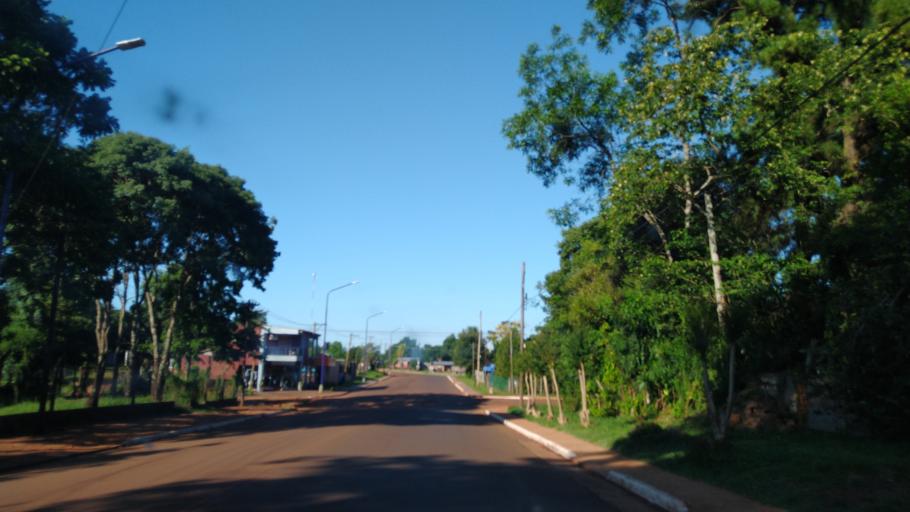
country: AR
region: Misiones
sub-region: Departamento de San Ignacio
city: San Ignacio
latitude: -27.2507
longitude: -55.5312
